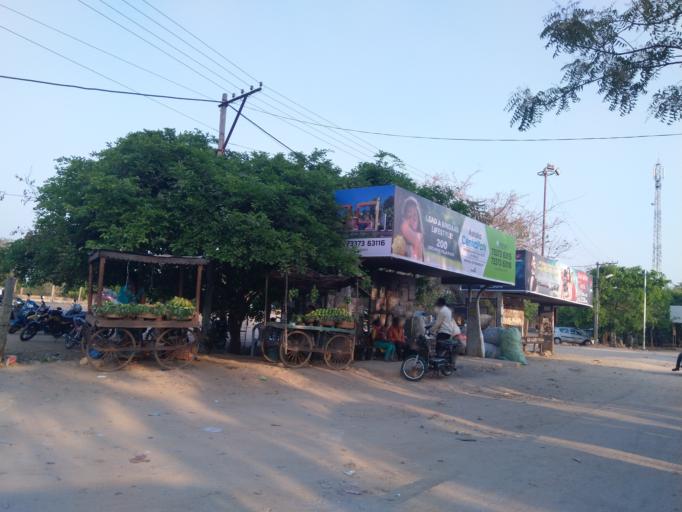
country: IN
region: Telangana
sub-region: Rangareddi
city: Sriramnagar
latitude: 17.3573
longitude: 78.2998
